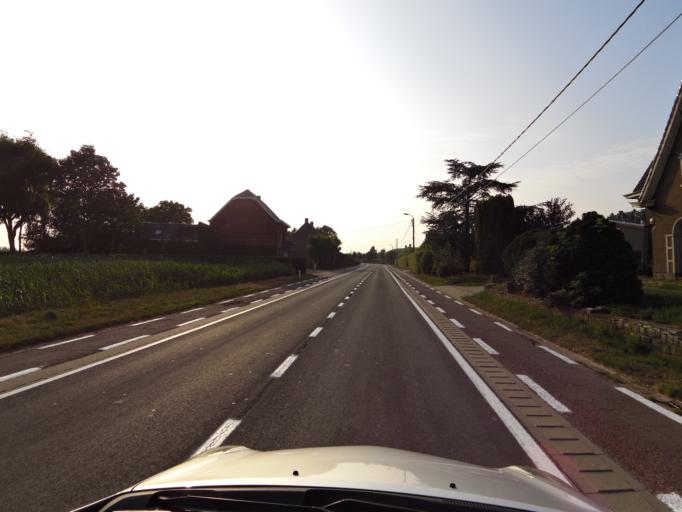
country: BE
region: Flanders
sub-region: Provincie West-Vlaanderen
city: Ardooie
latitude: 51.0009
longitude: 3.2185
